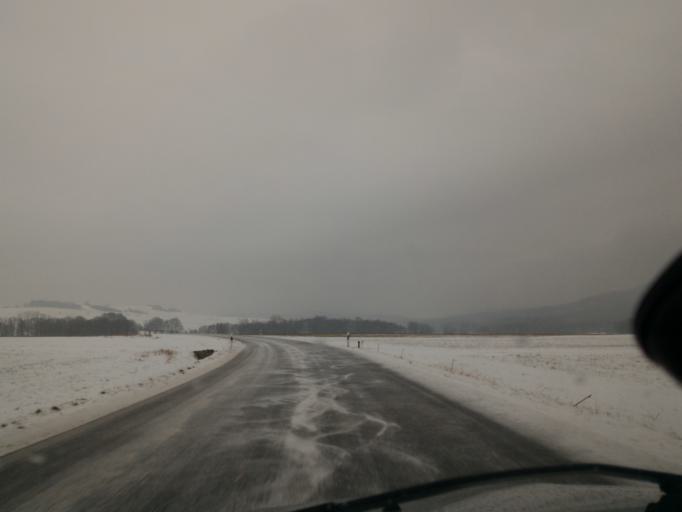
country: DE
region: Saxony
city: Grossschonau
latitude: 50.8784
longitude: 14.6757
